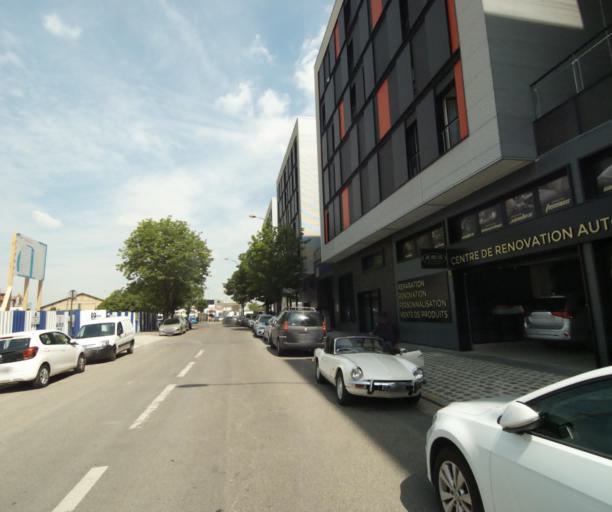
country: FR
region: Ile-de-France
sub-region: Departement des Hauts-de-Seine
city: Clichy
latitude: 48.9182
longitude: 2.3145
